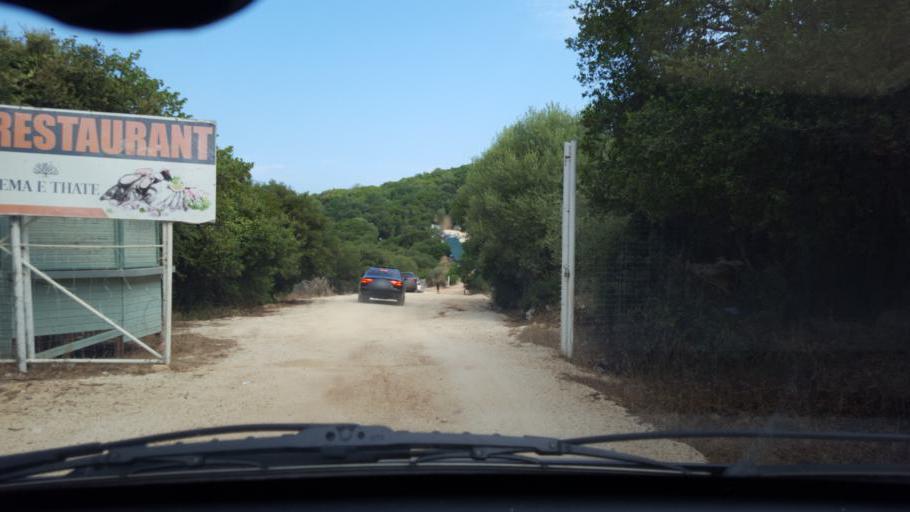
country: AL
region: Vlore
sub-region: Rrethi i Sarandes
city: Xarre
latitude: 39.7474
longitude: 19.9770
